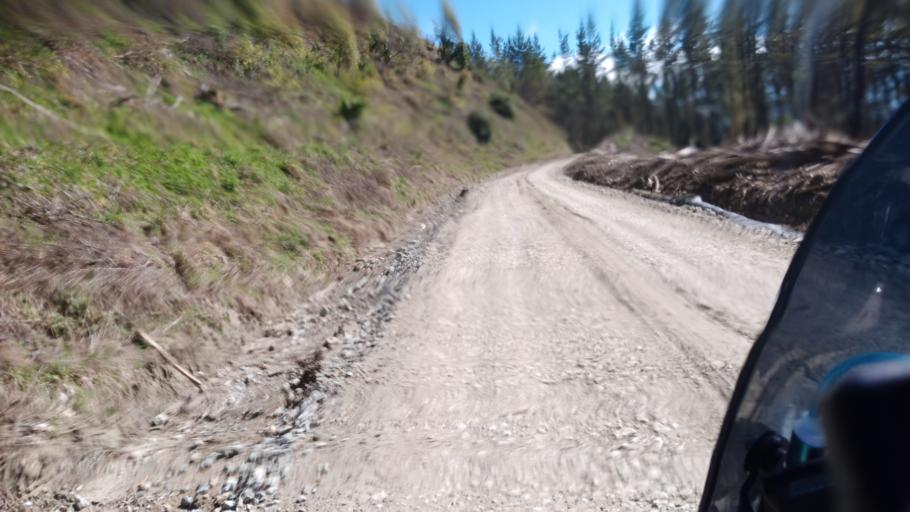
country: NZ
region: Gisborne
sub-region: Gisborne District
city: Gisborne
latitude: -38.8973
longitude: 177.8018
